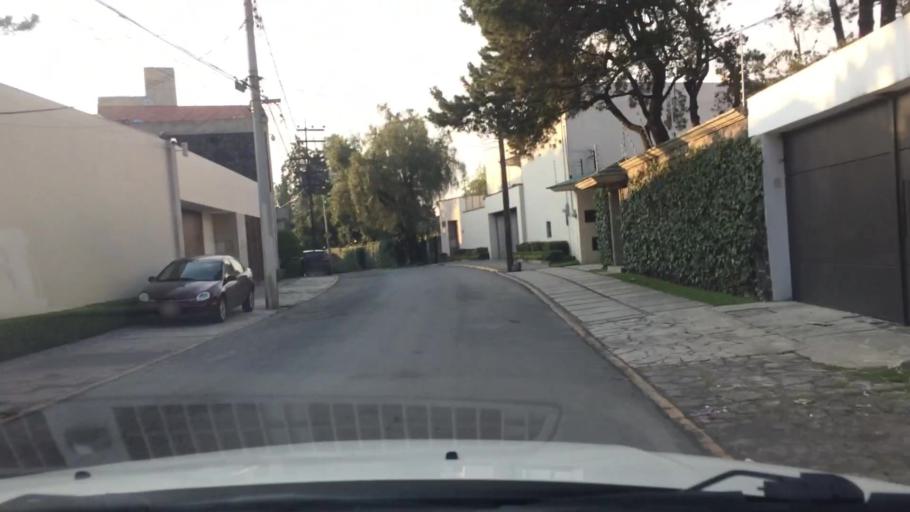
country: MX
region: Mexico City
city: Magdalena Contreras
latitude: 19.3195
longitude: -99.2090
